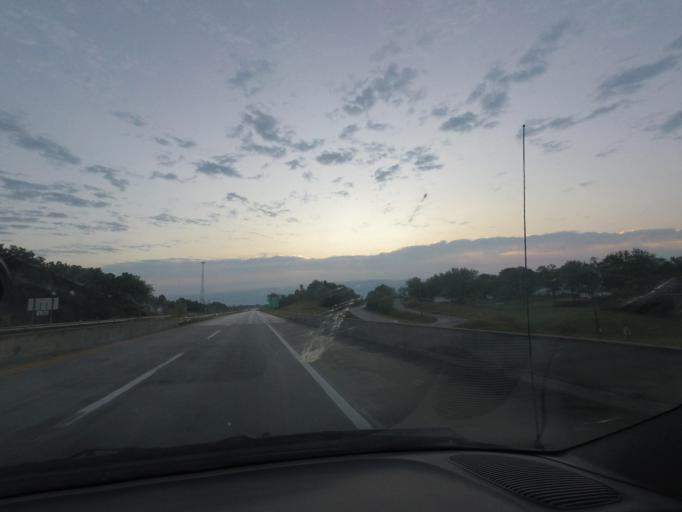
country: US
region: Missouri
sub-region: Macon County
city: Macon
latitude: 39.7518
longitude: -92.4743
